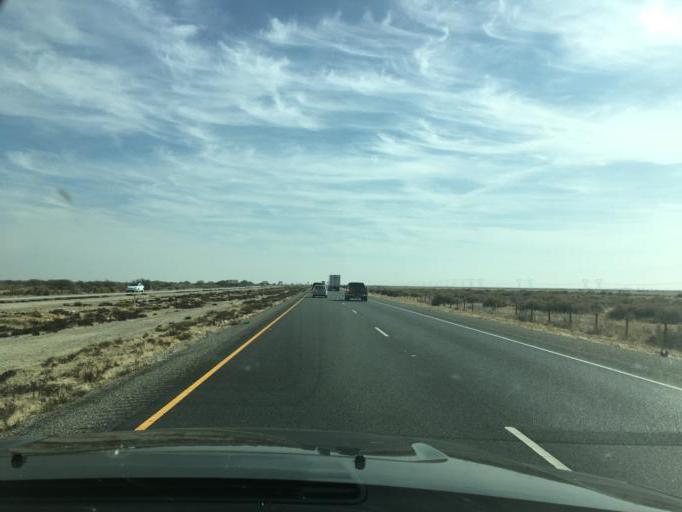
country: US
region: California
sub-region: Kern County
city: Buttonwillow
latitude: 35.3518
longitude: -119.3318
